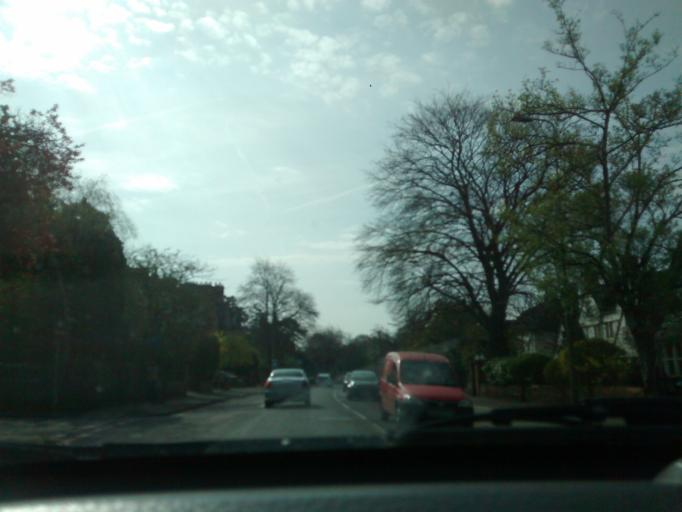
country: GB
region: England
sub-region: Oxfordshire
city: Oxford
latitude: 51.7751
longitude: -1.2681
